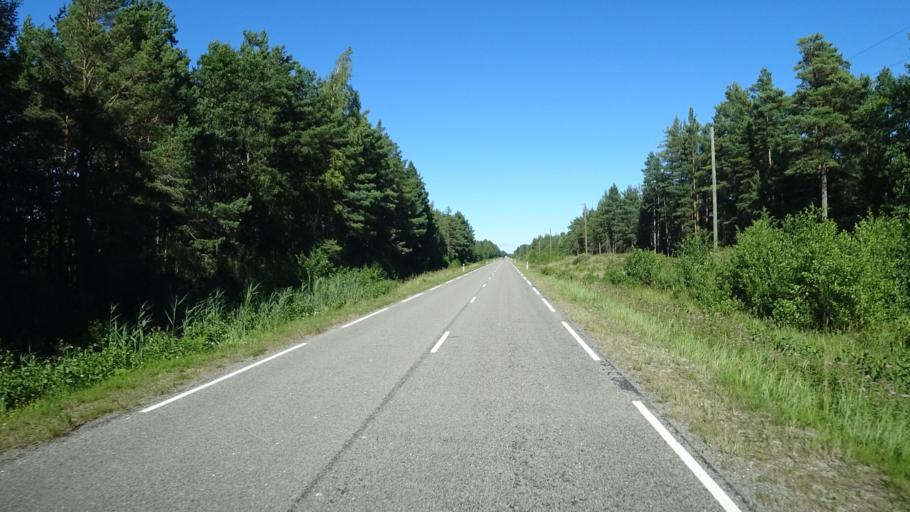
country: LV
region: Dundaga
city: Dundaga
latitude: 57.7007
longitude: 22.4202
